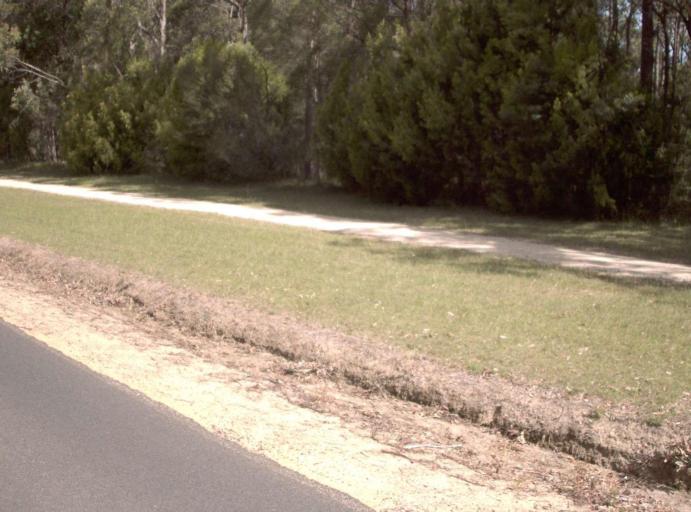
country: AU
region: New South Wales
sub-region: Bega Valley
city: Eden
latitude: -37.5553
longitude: 149.7442
